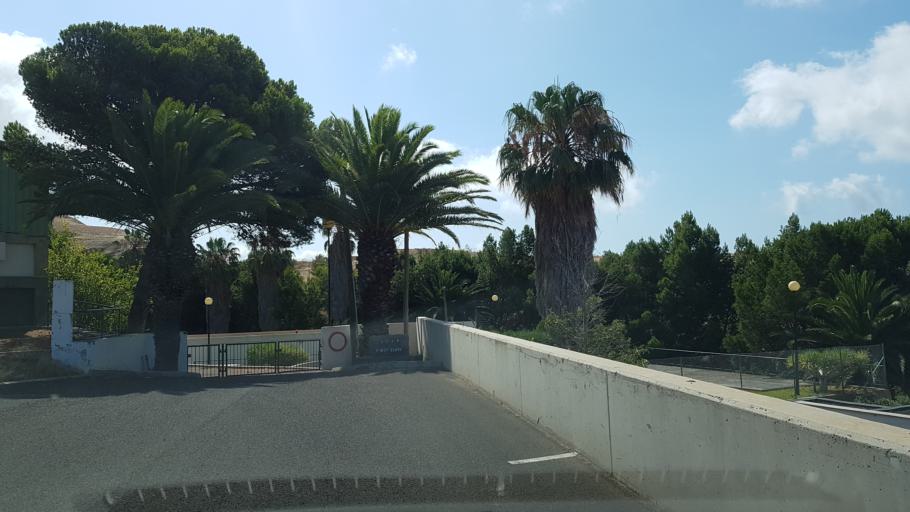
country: PT
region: Madeira
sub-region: Porto Santo
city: Vila de Porto Santo
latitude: 33.0652
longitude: -16.3267
